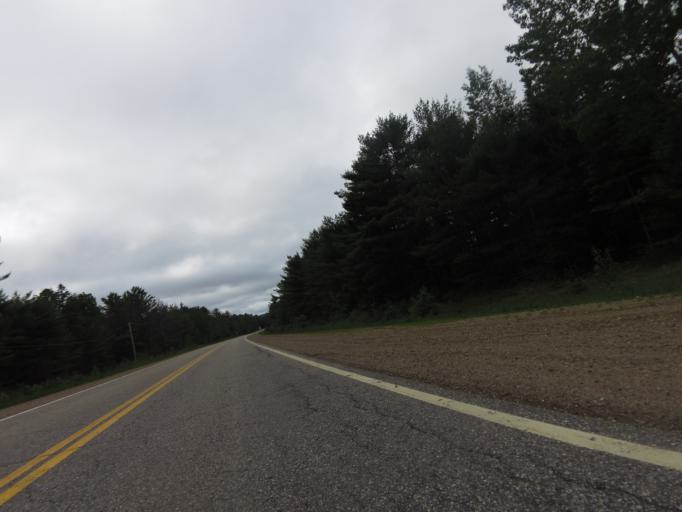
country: CA
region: Quebec
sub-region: Outaouais
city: Shawville
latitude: 45.8633
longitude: -76.4079
